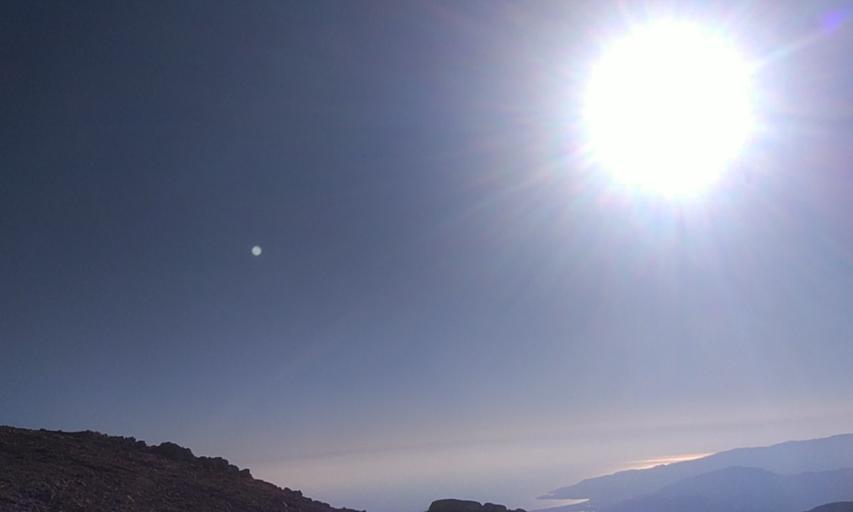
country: TR
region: Antalya
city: Altinyaka
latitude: 36.5382
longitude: 30.4401
